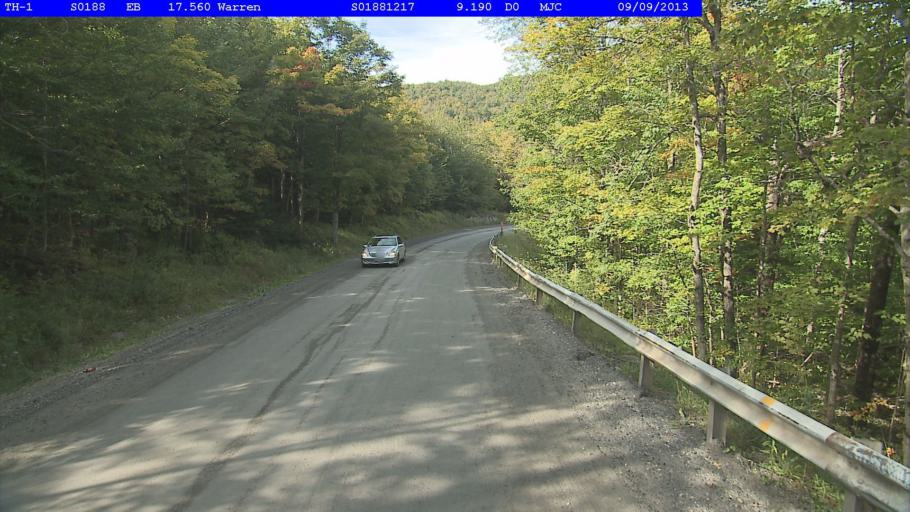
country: US
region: Vermont
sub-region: Washington County
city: Northfield
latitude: 44.1122
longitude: -72.7835
